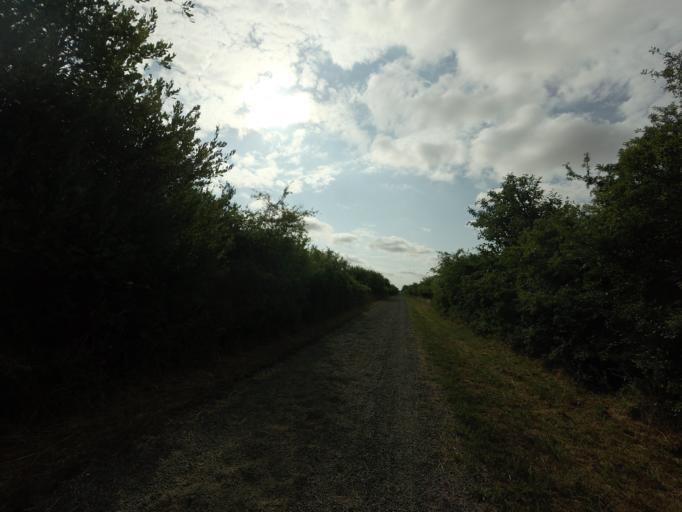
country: SE
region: Skane
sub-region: Helsingborg
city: Odakra
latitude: 56.1646
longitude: 12.7351
